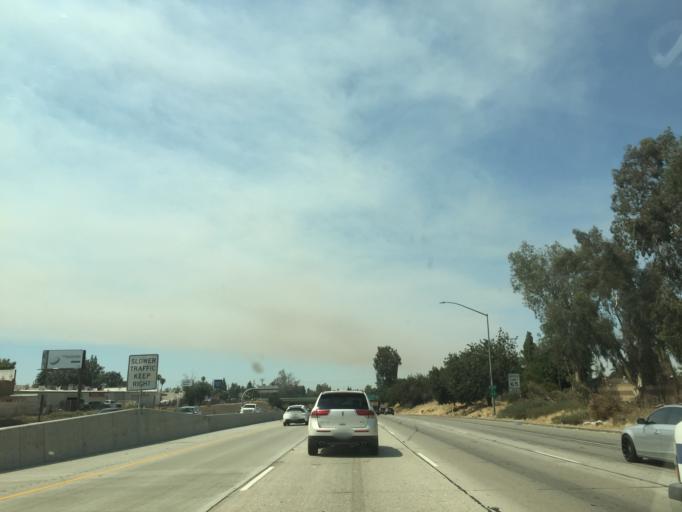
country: US
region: California
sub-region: Kern County
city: Bakersfield
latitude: 35.3222
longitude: -119.0373
